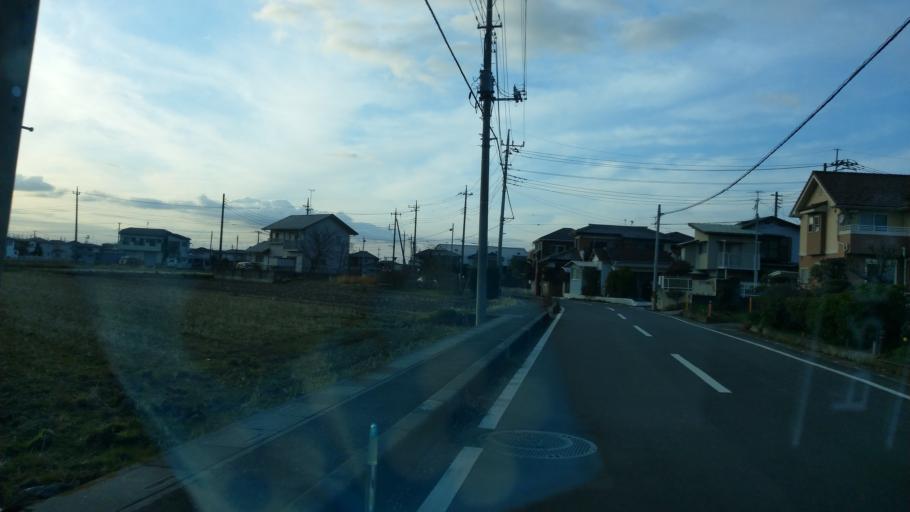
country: JP
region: Saitama
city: Yono
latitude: 35.8889
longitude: 139.5843
